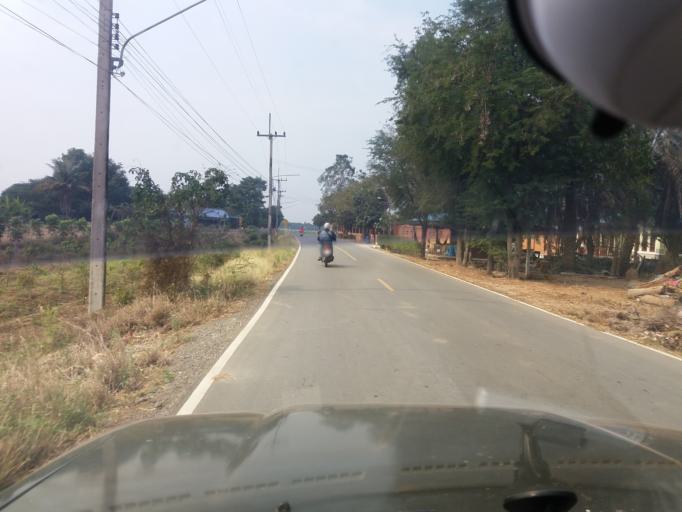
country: TH
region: Suphan Buri
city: Doem Bang Nang Buat
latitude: 14.8922
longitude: 100.1640
